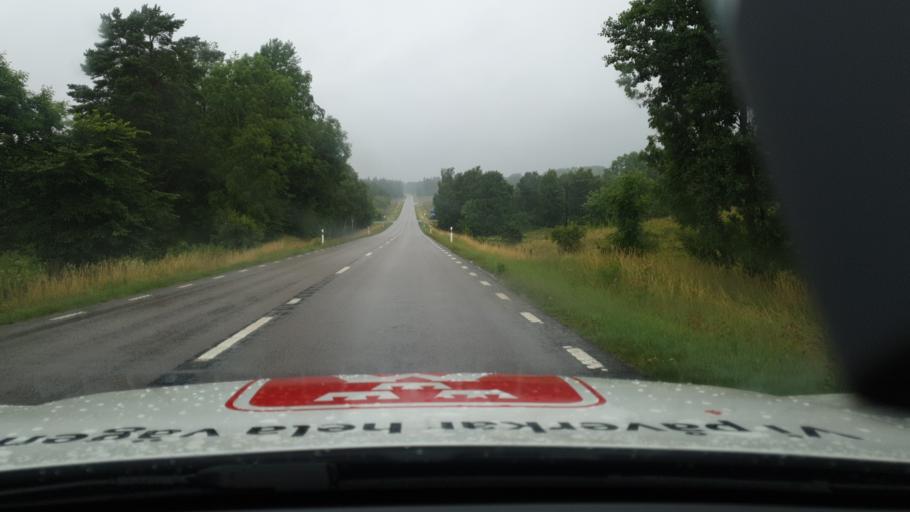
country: SE
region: Vaestra Goetaland
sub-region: Falkopings Kommun
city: Floby
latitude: 58.1703
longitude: 13.4068
